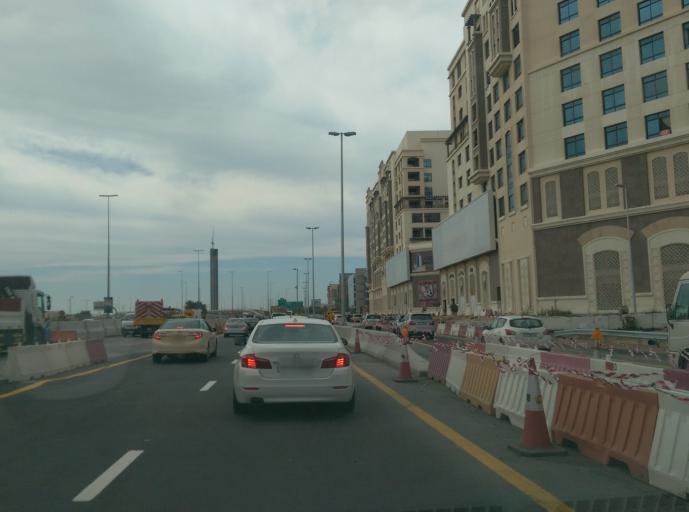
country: AE
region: Ash Shariqah
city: Sharjah
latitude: 25.2305
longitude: 55.3138
